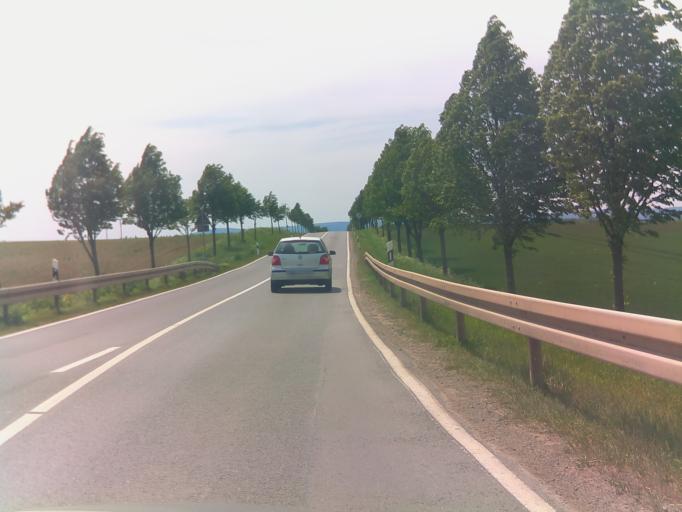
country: DE
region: Saxony-Anhalt
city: Hedersleben
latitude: 51.8308
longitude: 11.2341
